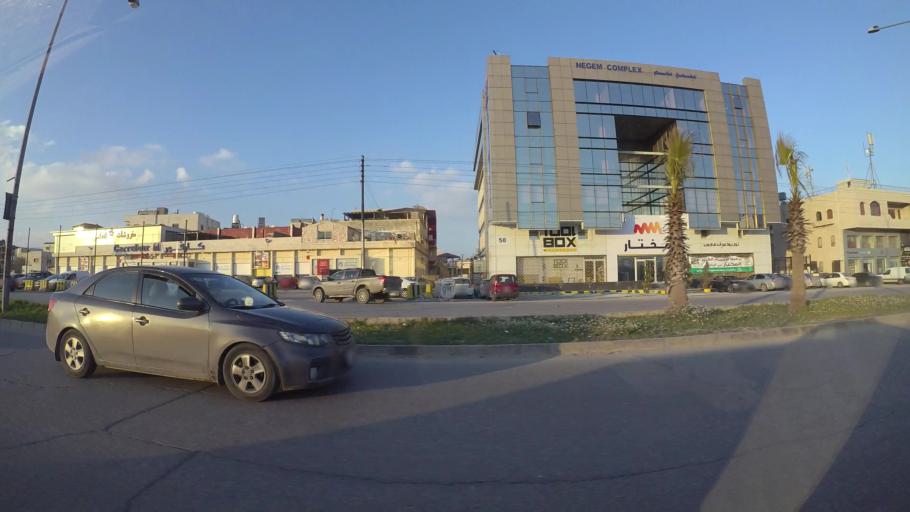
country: JO
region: Amman
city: Al Quwaysimah
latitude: 31.9077
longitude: 35.9306
